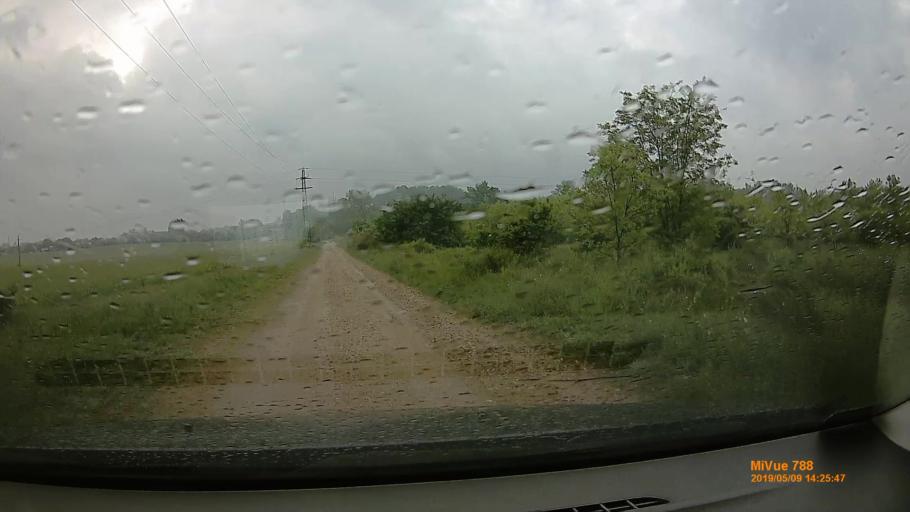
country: HU
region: Budapest
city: Budapest XVII. keruelet
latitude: 47.4961
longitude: 19.2168
